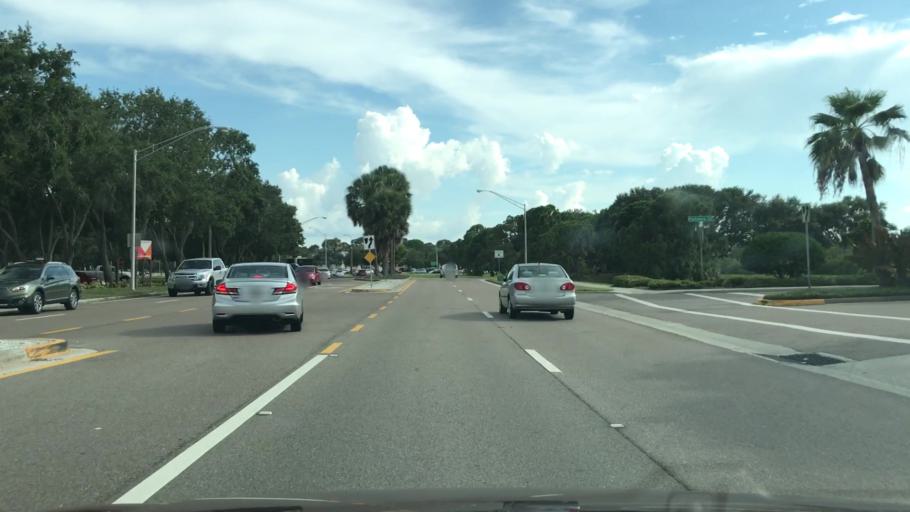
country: US
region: Florida
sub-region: Sarasota County
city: Venice Gardens
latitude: 27.0519
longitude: -82.3970
